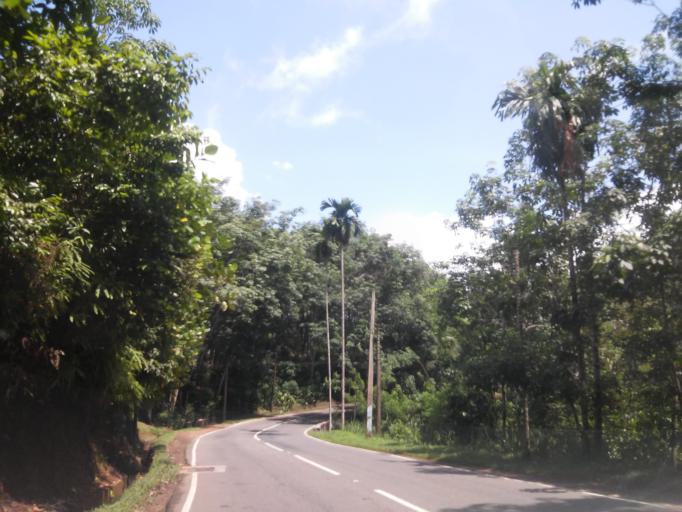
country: LK
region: Sabaragamuwa
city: Ratnapura
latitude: 6.7263
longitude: 80.3260
